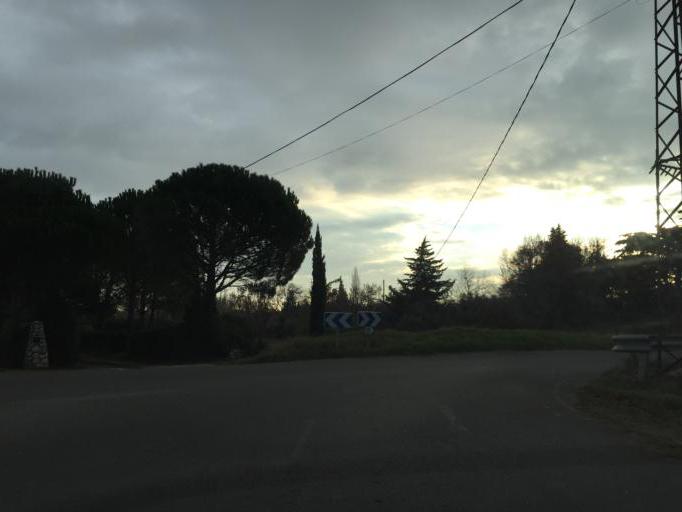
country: FR
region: Provence-Alpes-Cote d'Azur
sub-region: Departement du Vaucluse
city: Jonquieres
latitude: 44.1241
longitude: 4.8760
